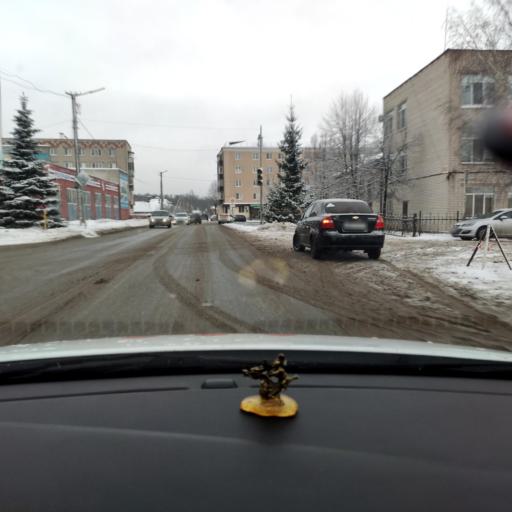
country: RU
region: Tatarstan
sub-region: Zelenodol'skiy Rayon
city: Zelenodolsk
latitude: 55.8553
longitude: 48.5309
